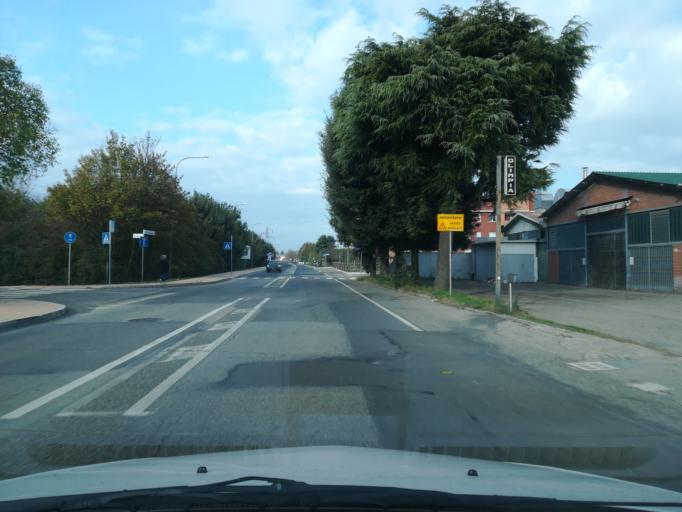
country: IT
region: Emilia-Romagna
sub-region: Provincia di Bologna
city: Imola
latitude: 44.3657
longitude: 11.7117
